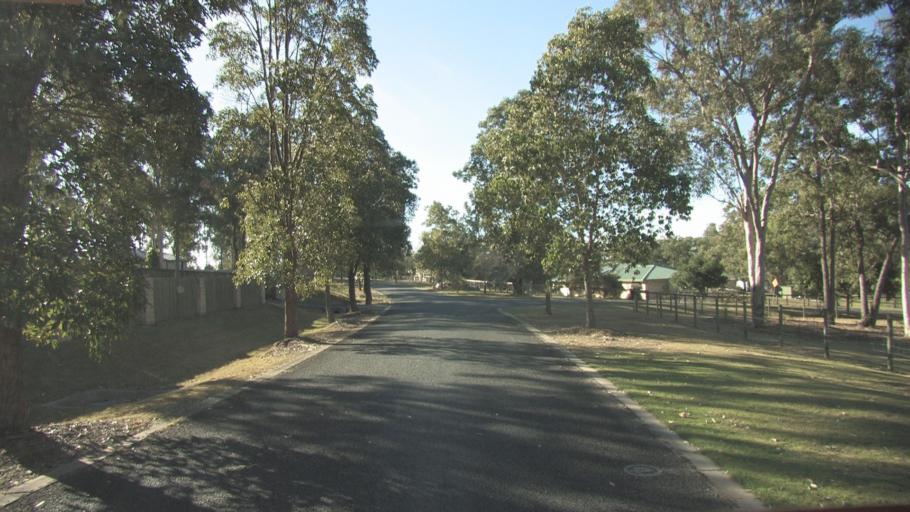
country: AU
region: Queensland
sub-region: Logan
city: North Maclean
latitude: -27.7340
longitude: 152.9710
